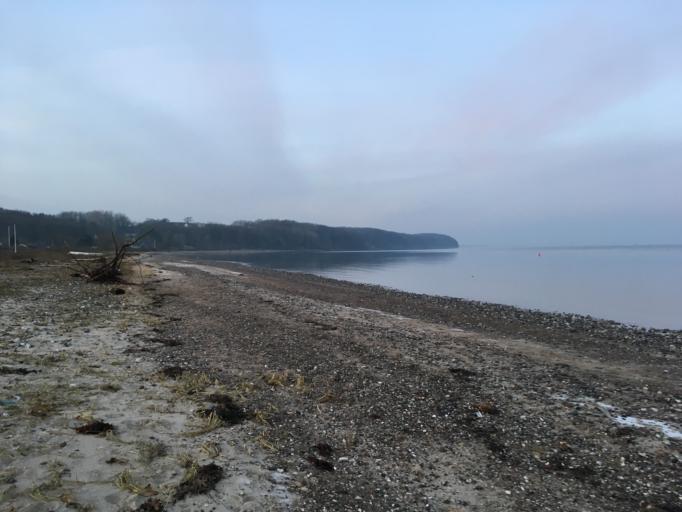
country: DK
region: South Denmark
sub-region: Middelfart Kommune
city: Norre Aby
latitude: 55.5214
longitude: 9.8526
